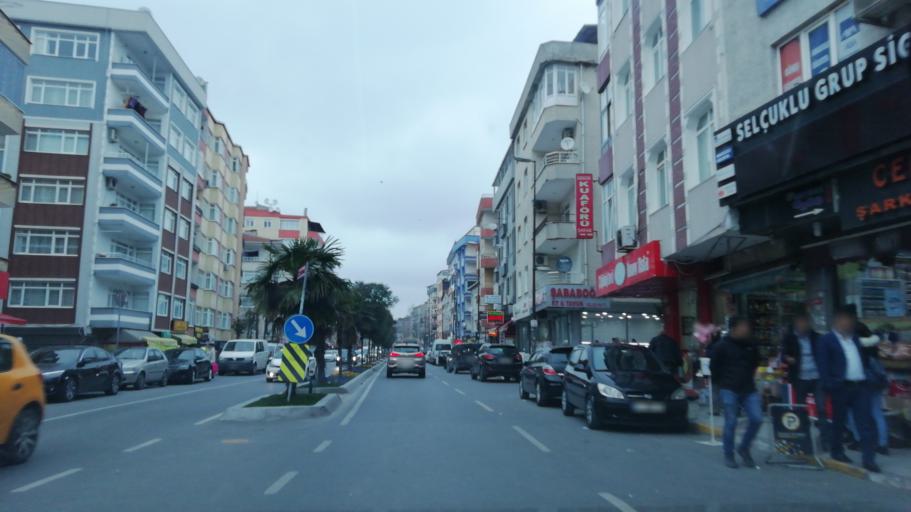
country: TR
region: Istanbul
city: Bahcelievler
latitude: 41.0063
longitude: 28.8494
